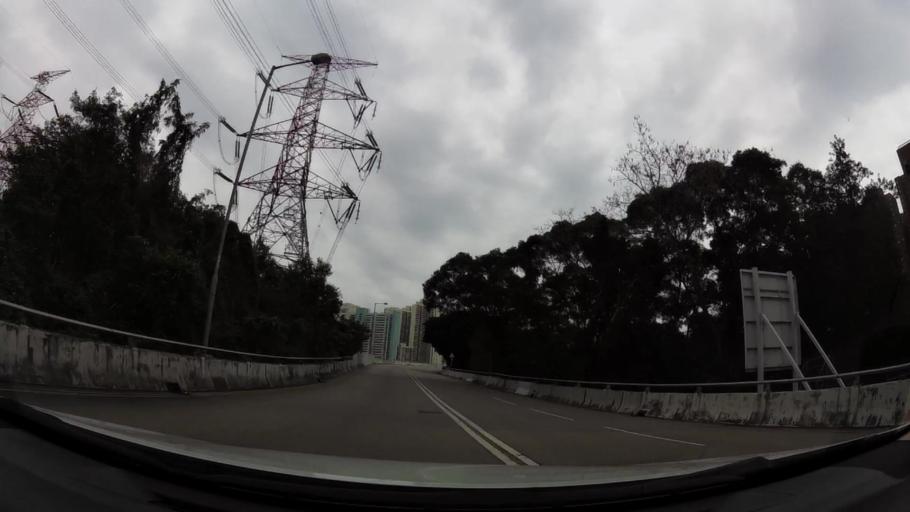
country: HK
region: Tuen Mun
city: Tuen Mun
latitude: 22.4155
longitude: 113.9784
